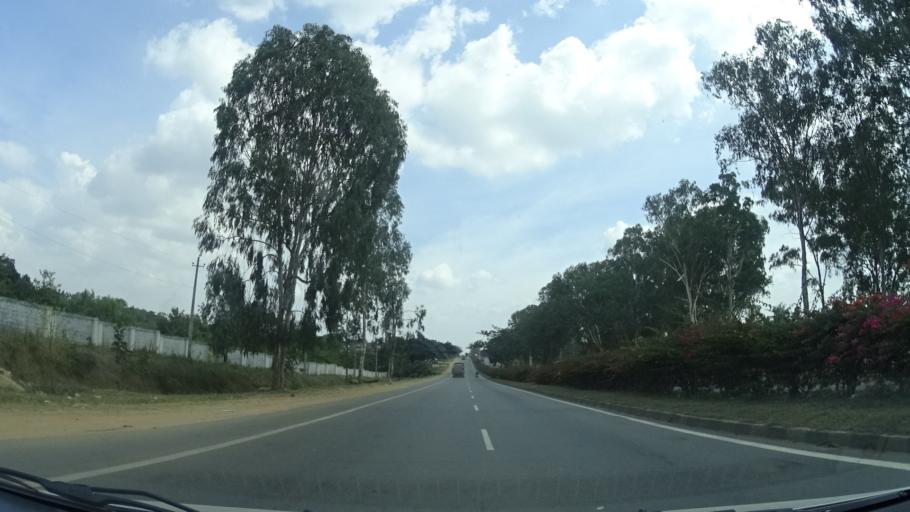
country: IN
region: Karnataka
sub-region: Bangalore Rural
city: Nelamangala
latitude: 13.1639
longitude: 77.3178
